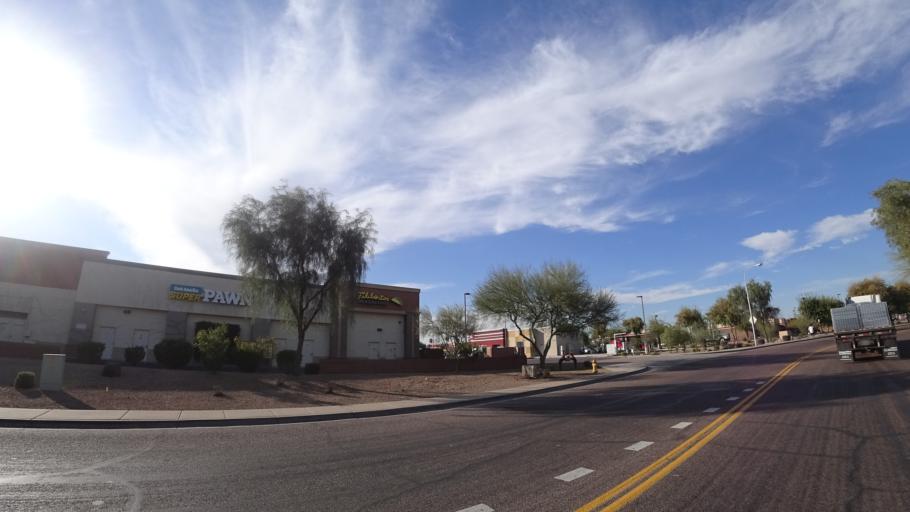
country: US
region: Arizona
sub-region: Maricopa County
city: Glendale
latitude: 33.4596
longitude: -112.1679
